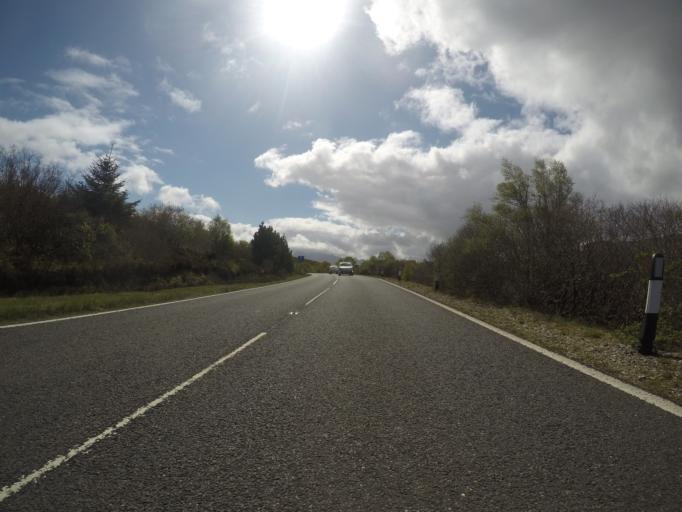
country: GB
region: Scotland
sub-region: Highland
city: Isle of Skye
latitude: 57.3453
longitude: -6.1976
